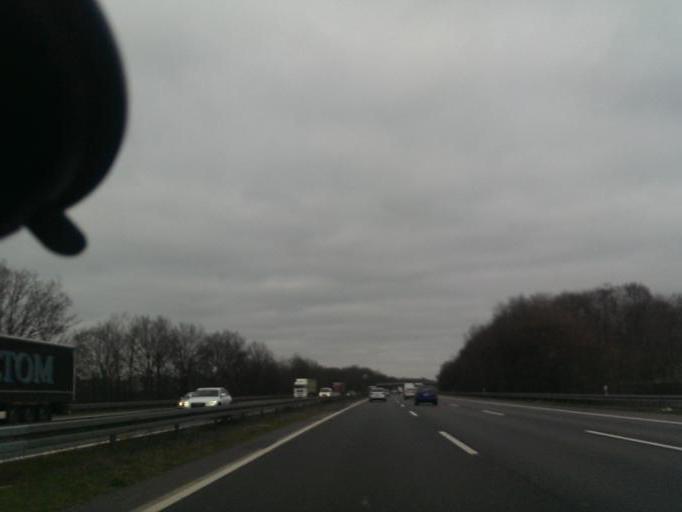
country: DE
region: North Rhine-Westphalia
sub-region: Regierungsbezirk Detmold
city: Verl
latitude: 51.8973
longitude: 8.4624
